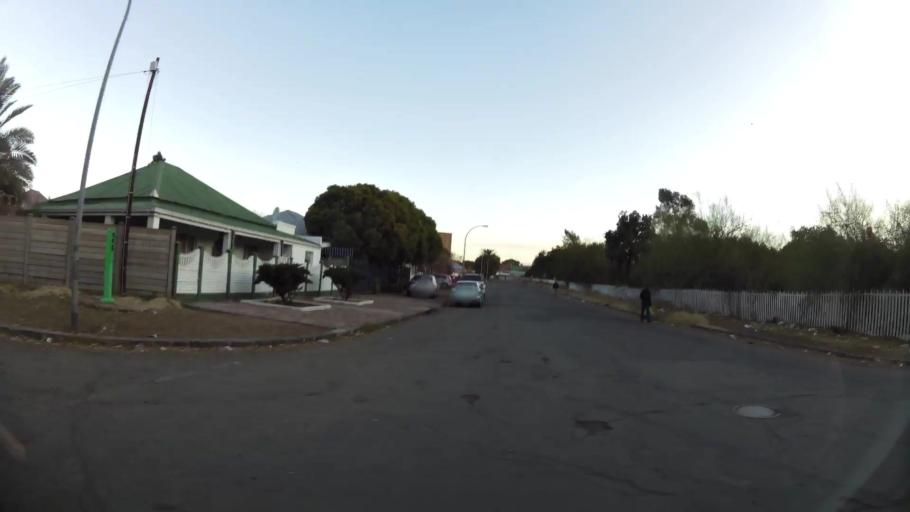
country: ZA
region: Northern Cape
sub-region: Frances Baard District Municipality
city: Kimberley
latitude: -28.7330
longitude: 24.7668
